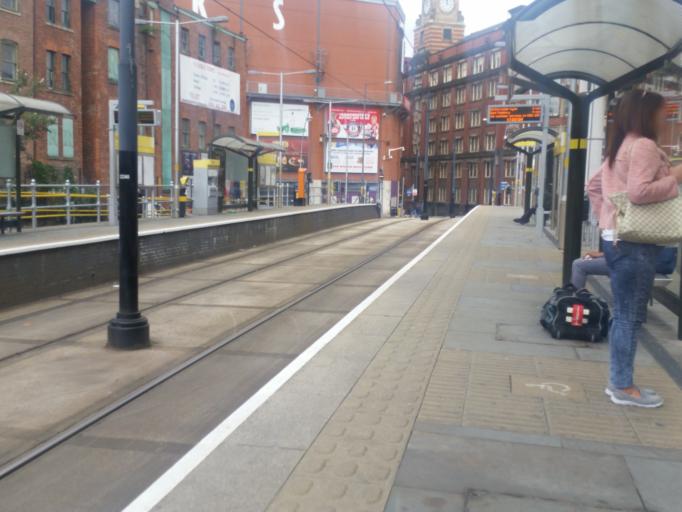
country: GB
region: England
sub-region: Manchester
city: Manchester
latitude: 53.4852
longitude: -2.2389
